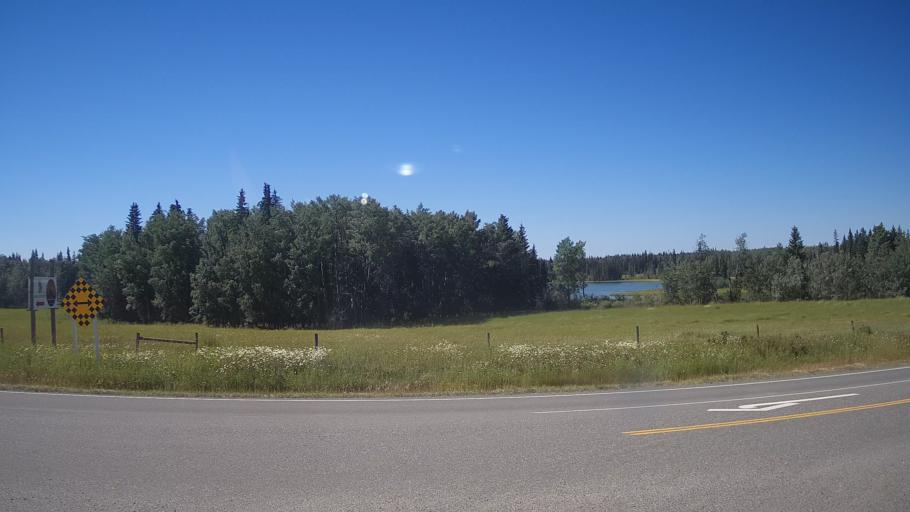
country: CA
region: British Columbia
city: Cache Creek
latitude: 51.5471
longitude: -120.9158
